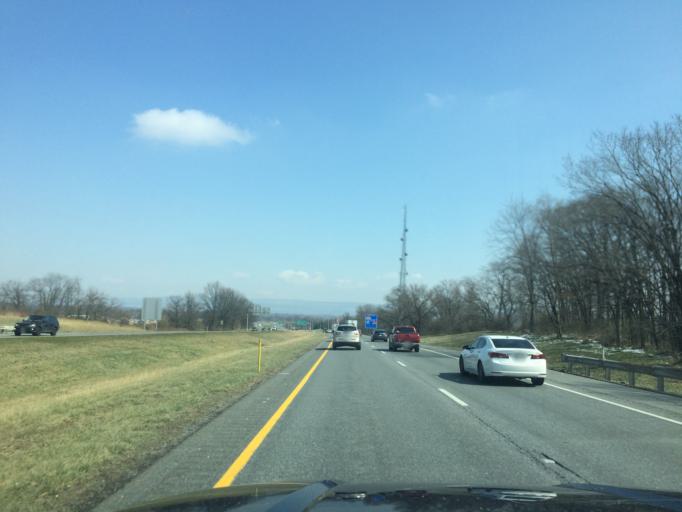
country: US
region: Maryland
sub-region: Washington County
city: Halfway
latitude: 39.6054
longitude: -77.7421
